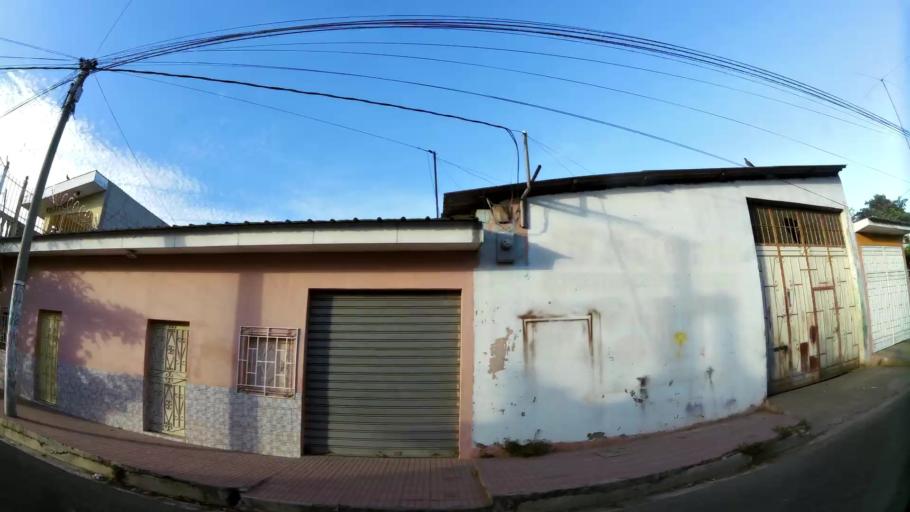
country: SV
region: Santa Ana
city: Metapan
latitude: 14.3289
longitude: -89.4445
